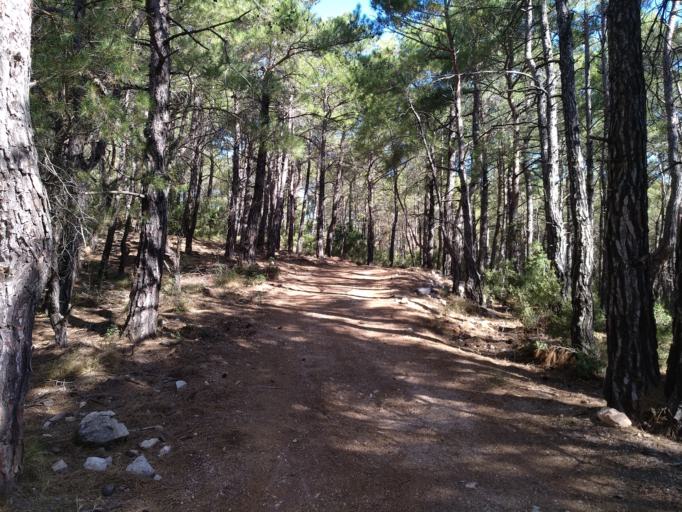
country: TR
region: Mugla
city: OEluedeniz
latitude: 36.5675
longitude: 29.1288
